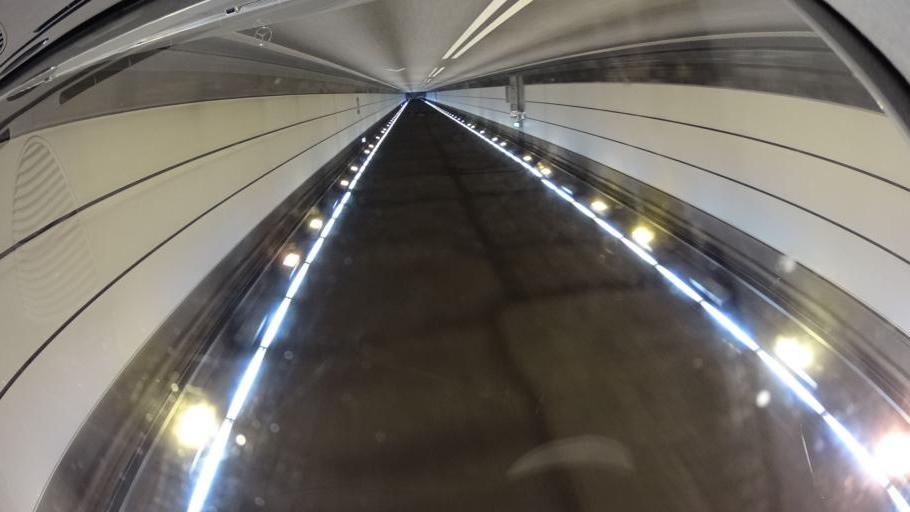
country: DK
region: Capital Region
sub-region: Dragor Kommune
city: Dragor
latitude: 55.6111
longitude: 12.7268
